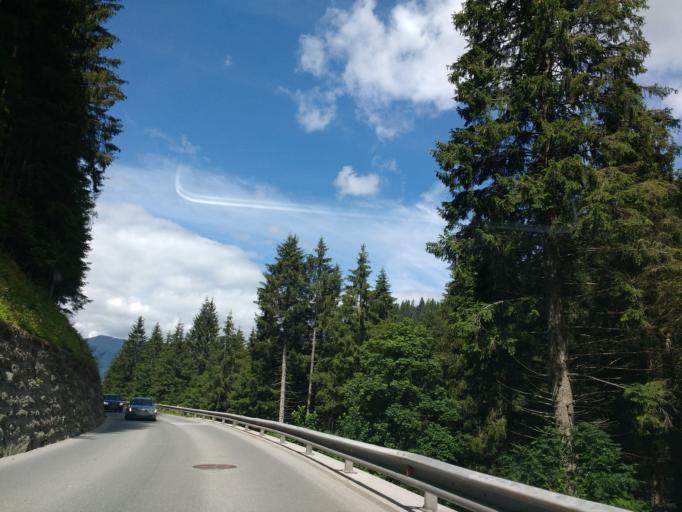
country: AT
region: Tyrol
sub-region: Politischer Bezirk Schwaz
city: Gerlos
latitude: 47.2087
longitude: 11.9697
